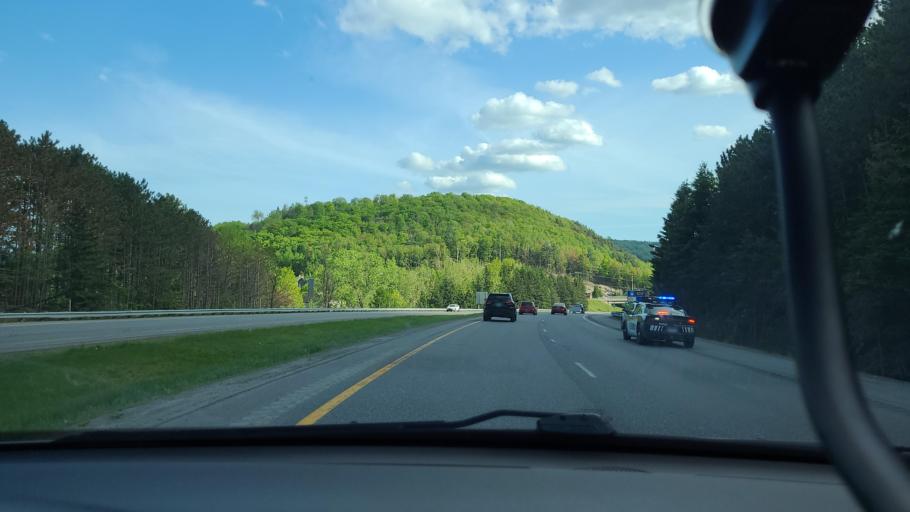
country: CA
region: Quebec
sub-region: Laurentides
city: Saint-Sauveur
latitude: 45.9042
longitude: -74.1419
